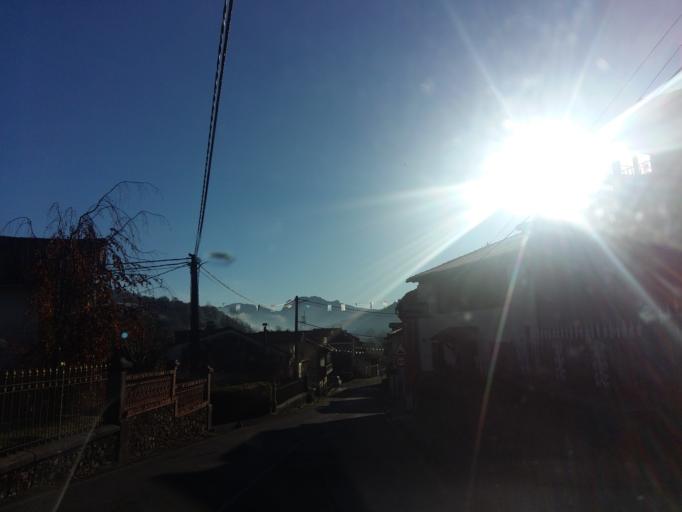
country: ES
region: Cantabria
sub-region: Provincia de Cantabria
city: Ramales de la Victoria
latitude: 43.2788
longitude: -3.5274
